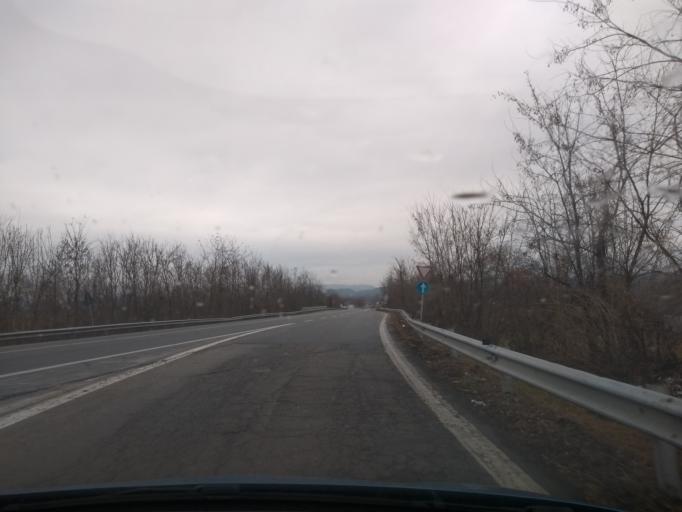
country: IT
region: Piedmont
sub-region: Provincia di Torino
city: Castellamonte
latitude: 45.3672
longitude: 7.7269
